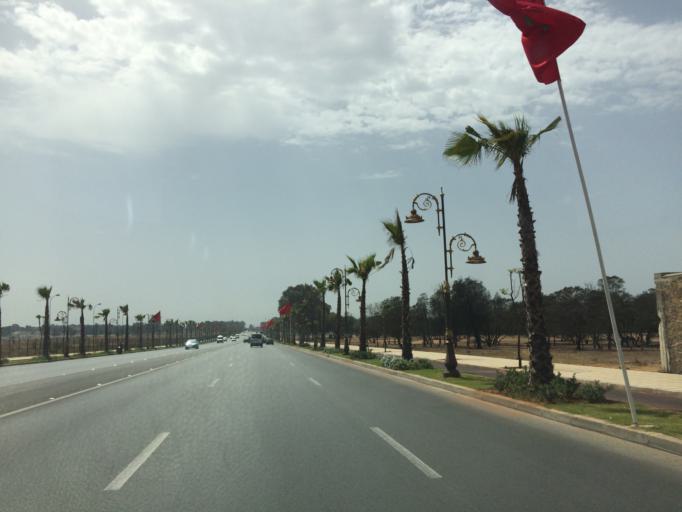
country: MA
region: Rabat-Sale-Zemmour-Zaer
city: Sale
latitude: 34.0322
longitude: -6.7656
